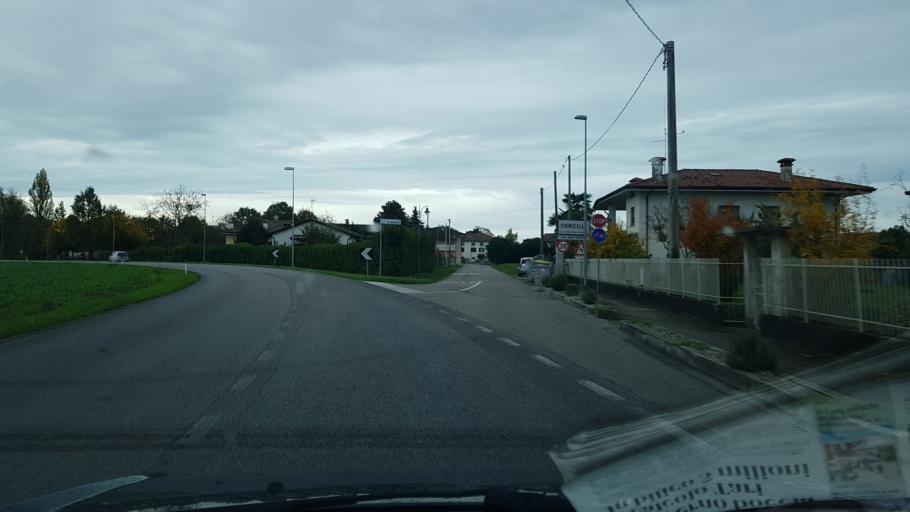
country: IT
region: Friuli Venezia Giulia
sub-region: Provincia di Udine
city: Villa Vicentina
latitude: 45.8039
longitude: 13.4005
